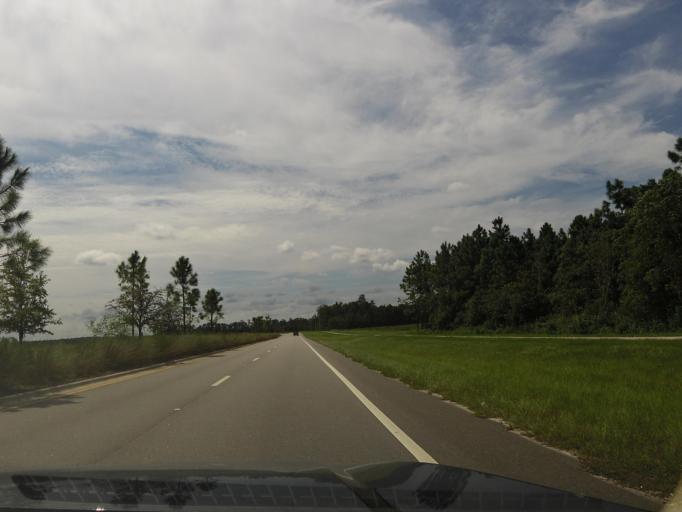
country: US
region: Florida
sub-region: Clay County
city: Green Cove Springs
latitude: 29.9909
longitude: -81.5115
